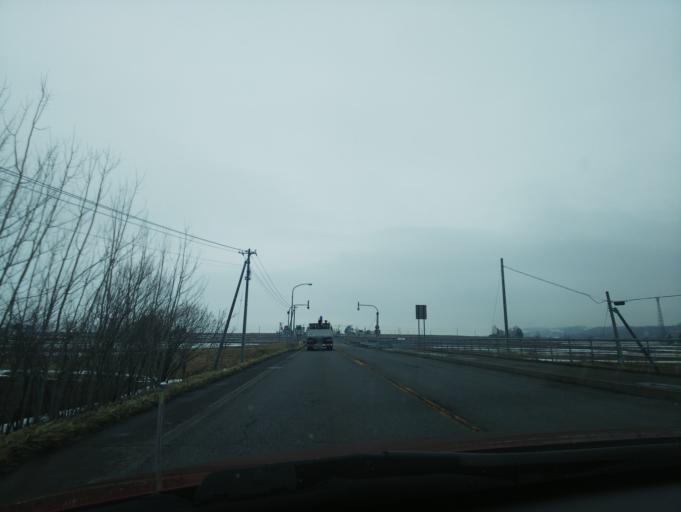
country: JP
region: Hokkaido
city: Nayoro
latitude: 44.0672
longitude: 142.3972
